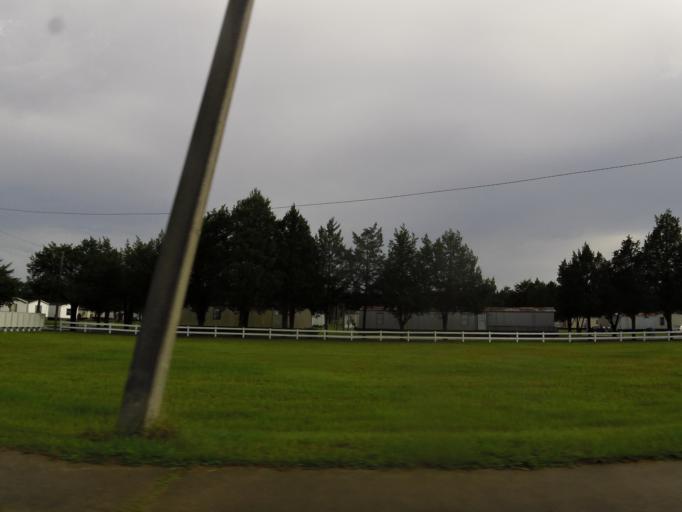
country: US
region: Georgia
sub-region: Liberty County
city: Walthourville
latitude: 31.7758
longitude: -81.6288
